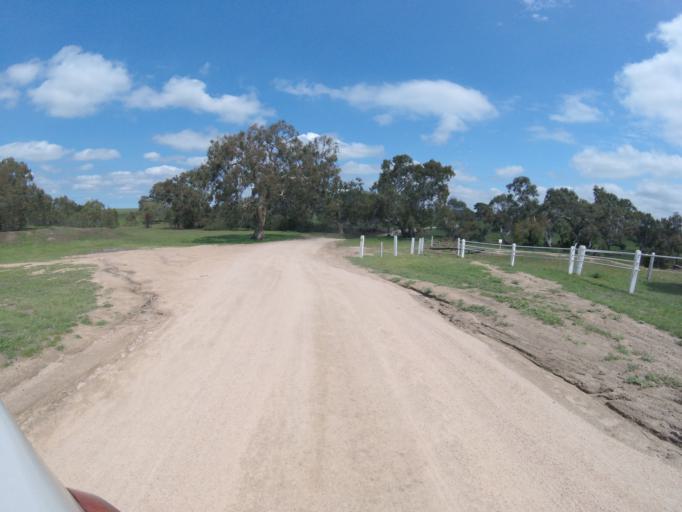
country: AU
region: Victoria
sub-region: Hume
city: Greenvale
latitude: -37.6409
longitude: 144.8384
